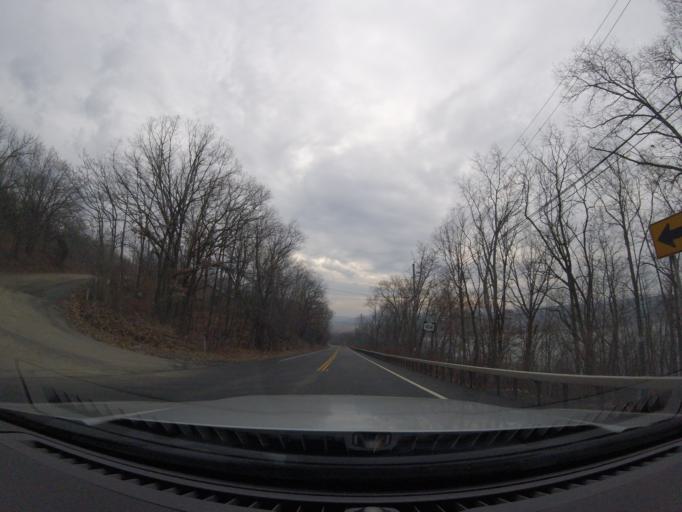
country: US
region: New York
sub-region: Schuyler County
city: Watkins Glen
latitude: 42.3983
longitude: -76.8578
